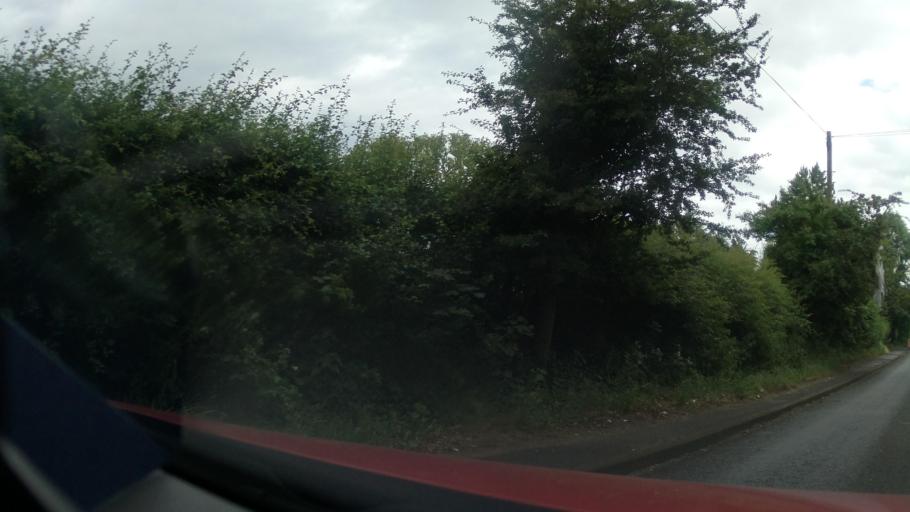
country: GB
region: England
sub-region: Dudley
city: Kingswinford
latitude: 52.5311
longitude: -2.1786
